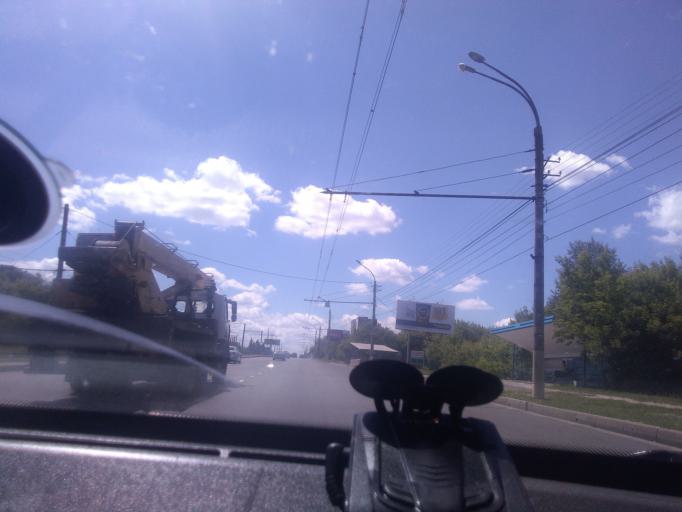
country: RU
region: Kursk
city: Kursk
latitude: 51.6826
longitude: 36.1497
